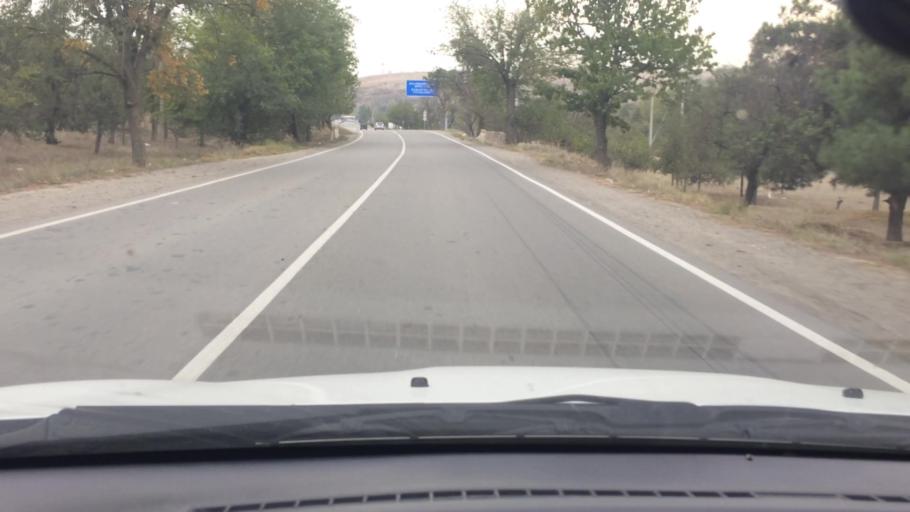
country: GE
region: Kvemo Kartli
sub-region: Gardabani
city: Gardabani
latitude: 41.3379
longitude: 45.0689
